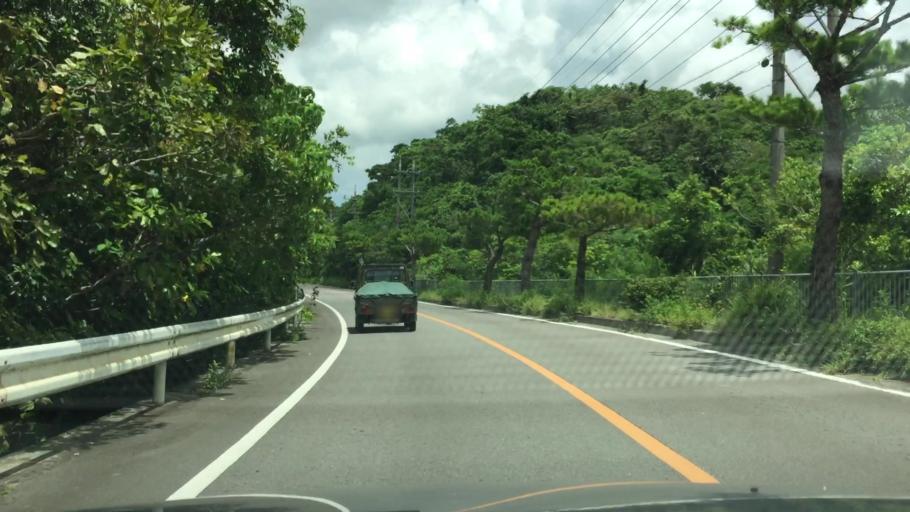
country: JP
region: Okinawa
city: Ishigaki
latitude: 24.3781
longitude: 124.1538
